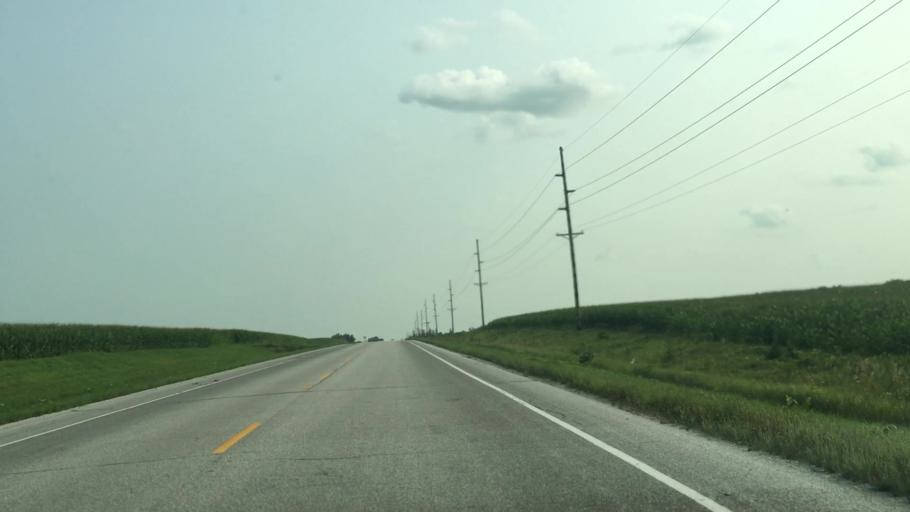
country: US
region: Minnesota
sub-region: Fillmore County
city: Harmony
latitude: 43.5617
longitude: -91.9298
